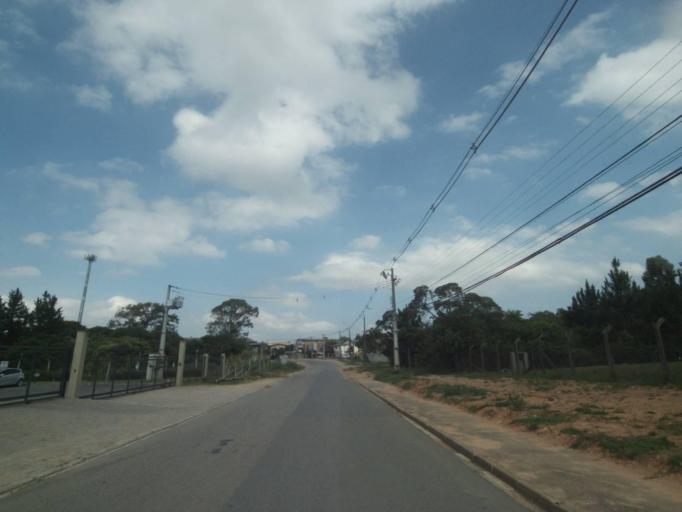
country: BR
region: Parana
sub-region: Curitiba
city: Curitiba
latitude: -25.5052
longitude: -49.3464
